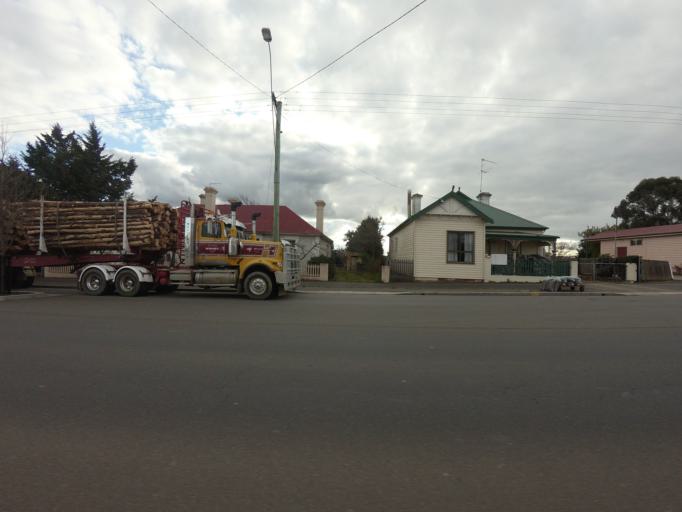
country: AU
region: Tasmania
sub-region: Northern Midlands
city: Evandale
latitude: -41.9320
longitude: 147.4930
